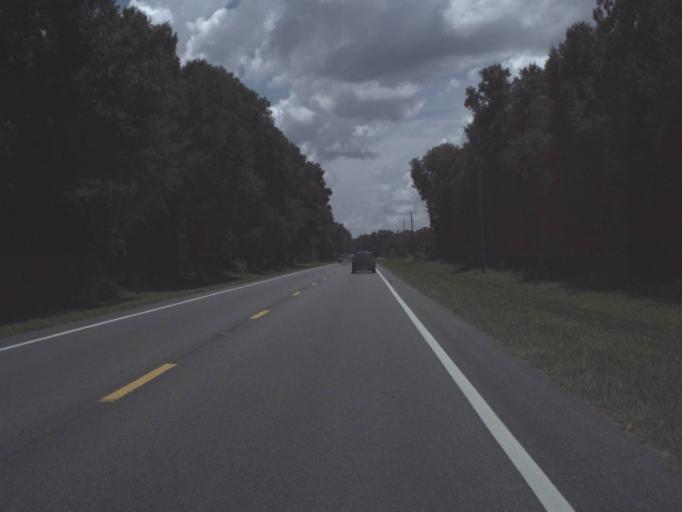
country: US
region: Florida
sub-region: Levy County
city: Manatee Road
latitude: 29.6001
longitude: -82.9234
